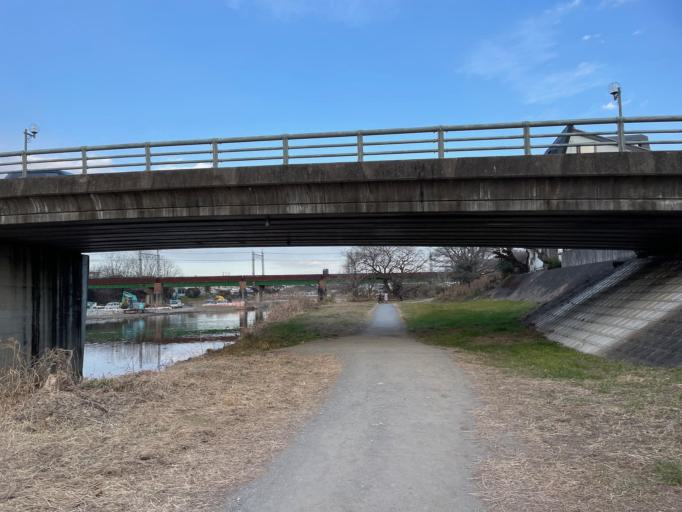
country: JP
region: Saitama
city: Hanno
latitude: 35.8380
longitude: 139.3479
